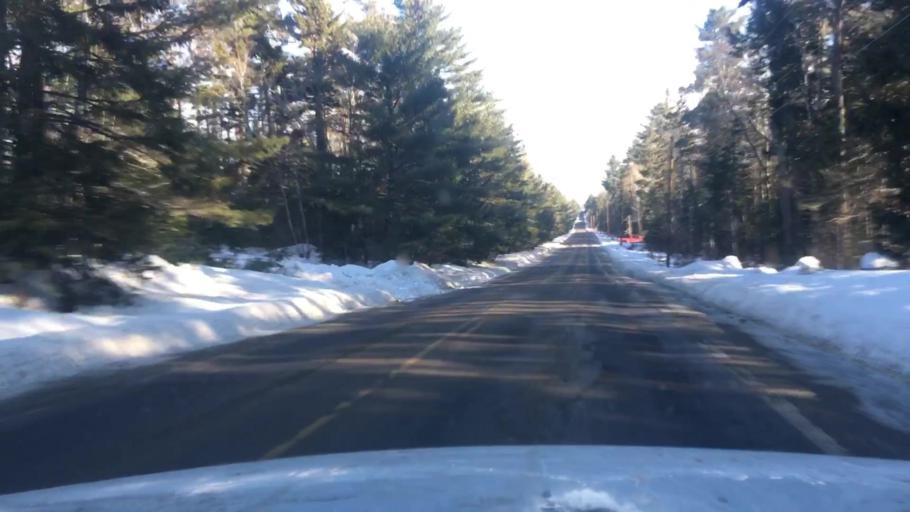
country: US
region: Maine
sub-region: Hancock County
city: Ellsworth
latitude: 44.6669
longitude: -68.3553
